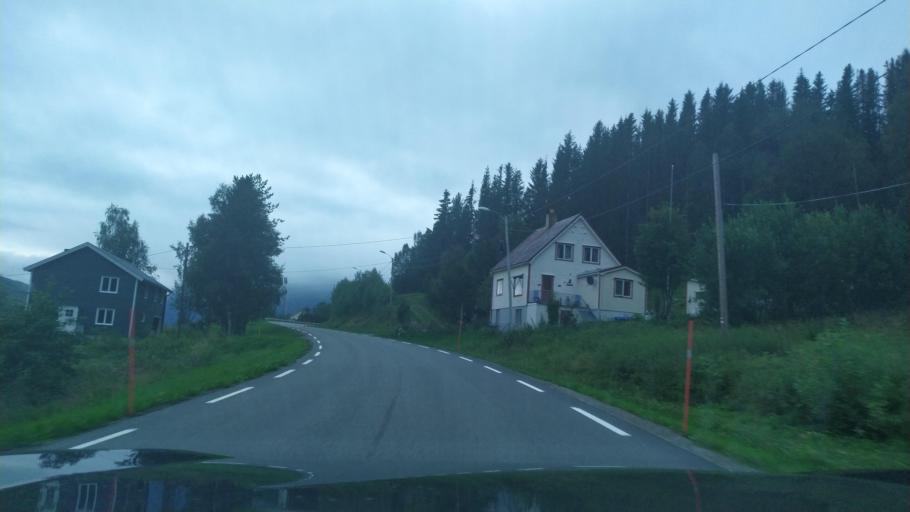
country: NO
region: Troms
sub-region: Lavangen
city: Tennevoll
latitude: 68.7506
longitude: 17.8155
